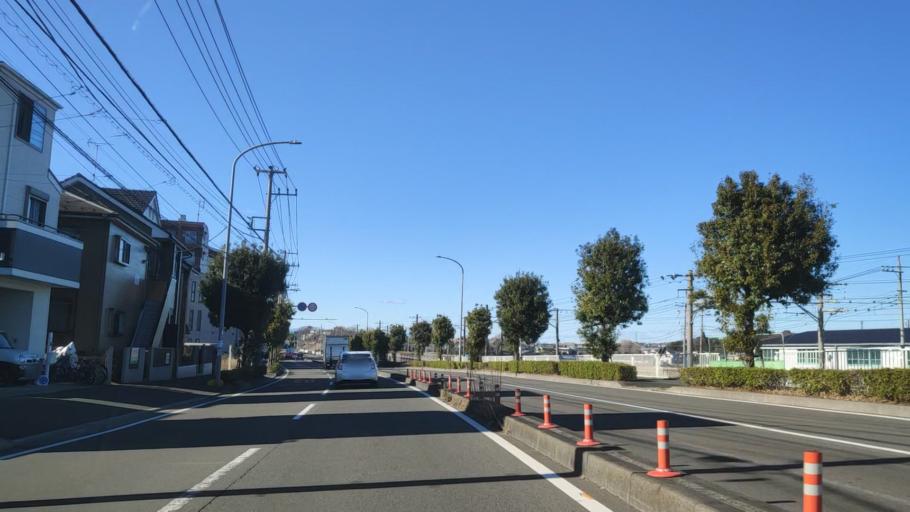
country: JP
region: Tokyo
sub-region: Machida-shi
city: Machida
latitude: 35.5175
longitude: 139.5335
